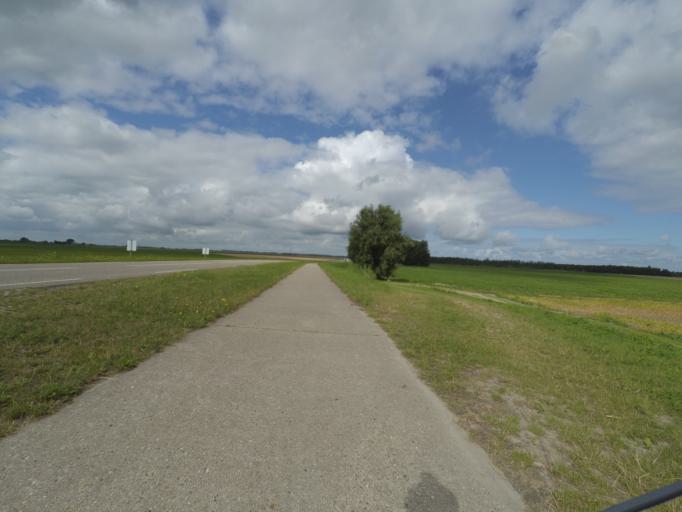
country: NL
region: Groningen
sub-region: Gemeente Zuidhorn
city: Grijpskerk
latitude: 53.3152
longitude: 6.2631
